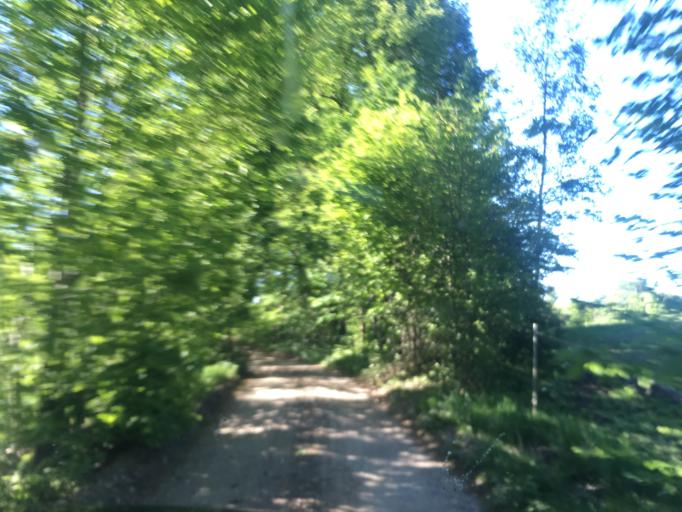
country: PL
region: Warmian-Masurian Voivodeship
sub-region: Powiat piski
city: Ruciane-Nida
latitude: 53.6564
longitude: 21.4833
